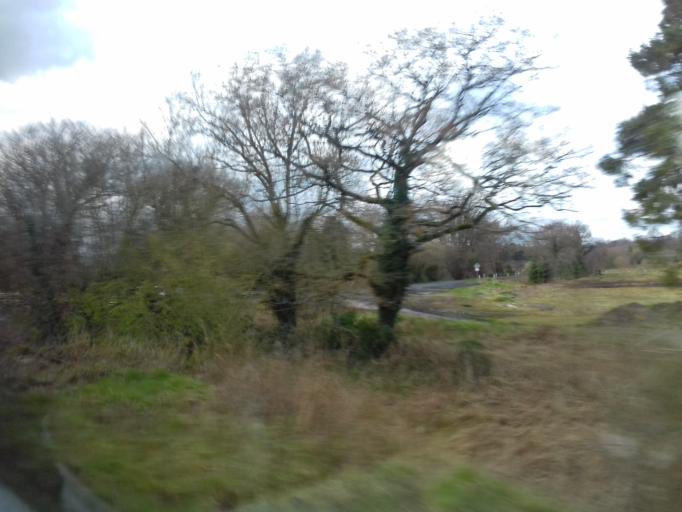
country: IE
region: Leinster
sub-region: An Iarmhi
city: Rochfortbridge
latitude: 53.4977
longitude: -7.2458
